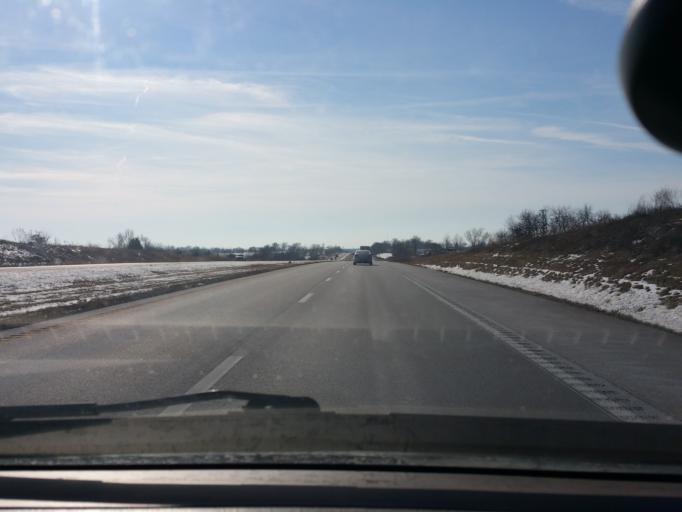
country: US
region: Missouri
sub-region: Clinton County
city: Cameron
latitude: 39.7978
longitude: -94.2017
